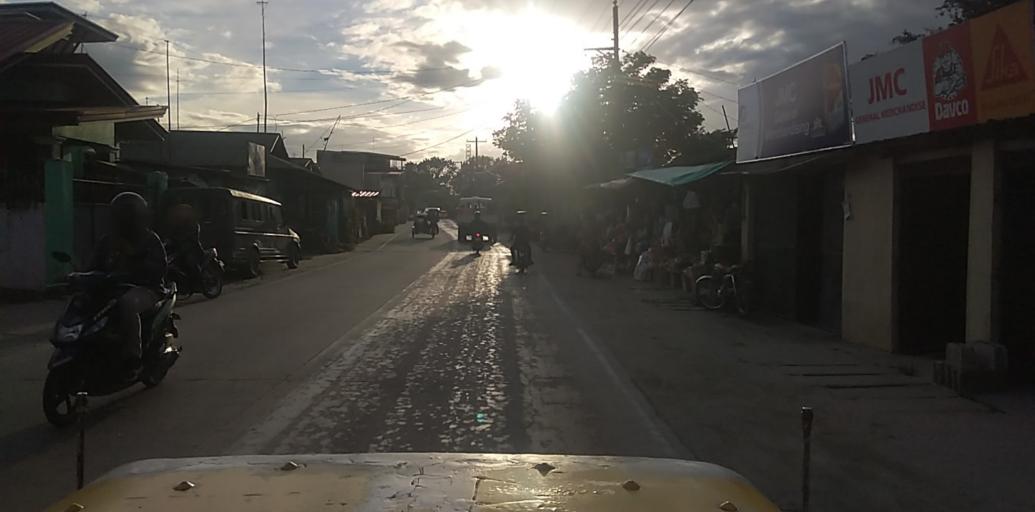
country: PH
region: Central Luzon
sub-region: Province of Pampanga
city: Malino
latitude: 15.1284
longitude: 120.6748
